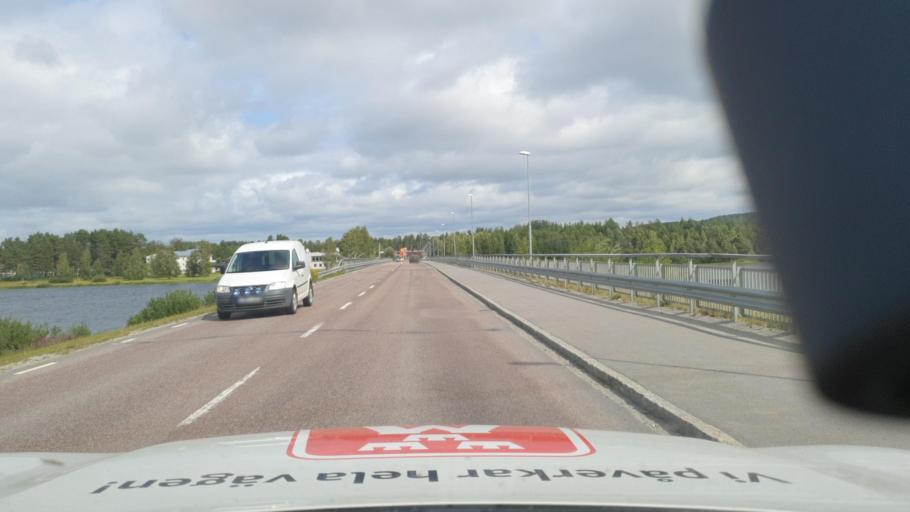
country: SE
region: Vaesterbotten
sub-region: Asele Kommun
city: Asele
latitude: 64.1647
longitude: 17.3613
